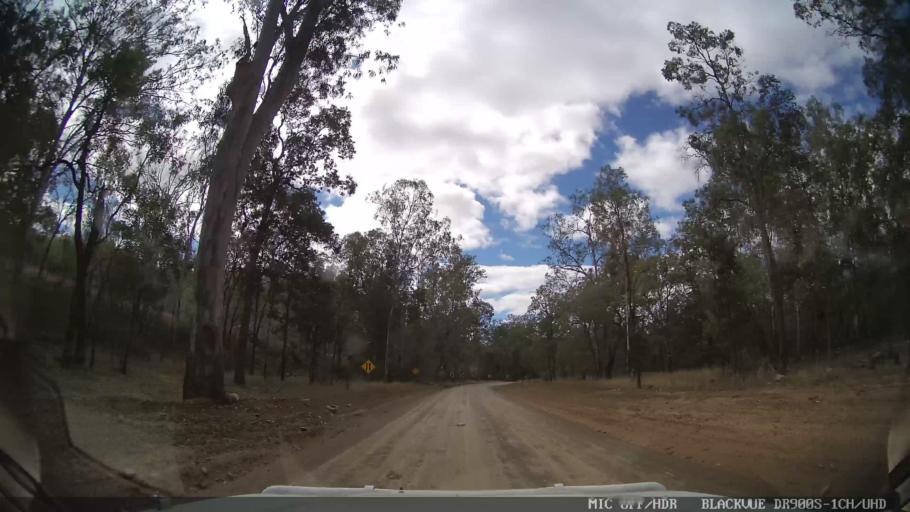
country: AU
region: Queensland
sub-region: Gladstone
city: Toolooa
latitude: -24.5482
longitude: 151.3436
